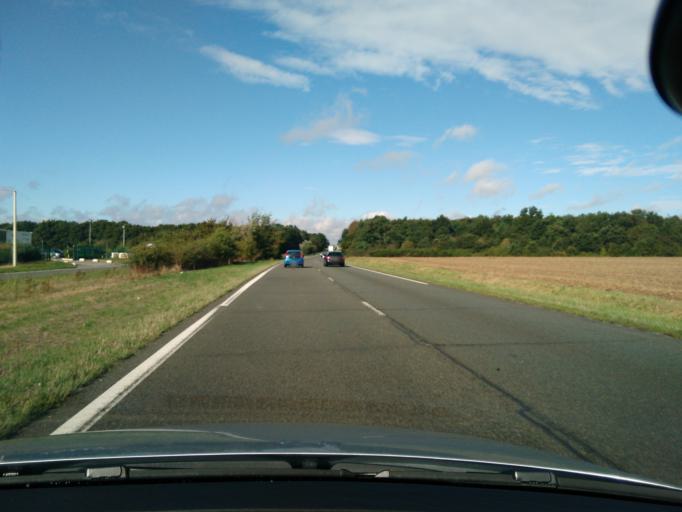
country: FR
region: Haute-Normandie
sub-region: Departement de l'Eure
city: Saint-Germain-sur-Avre
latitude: 48.7500
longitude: 1.2644
